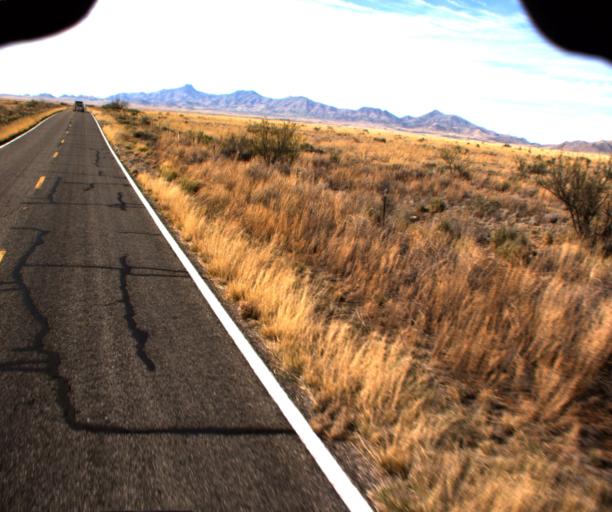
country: US
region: Arizona
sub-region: Cochise County
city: Willcox
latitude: 32.0409
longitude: -109.4819
